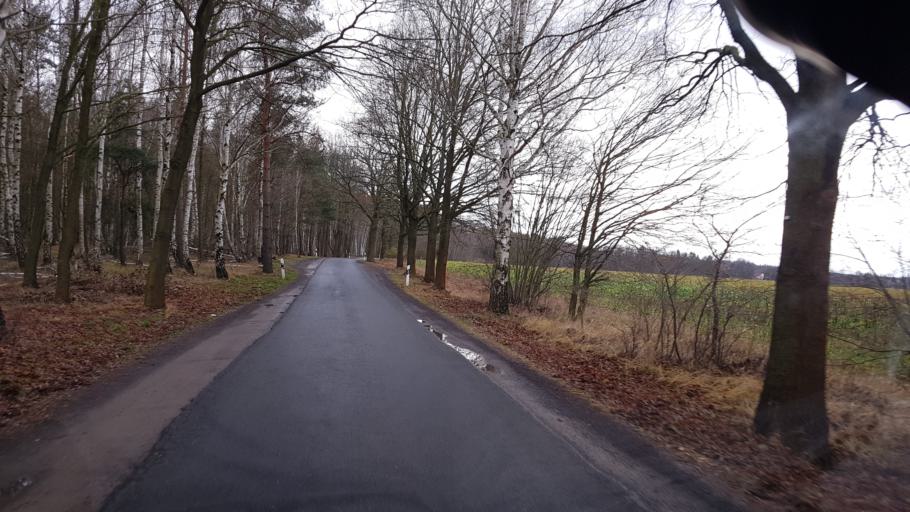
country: DE
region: Brandenburg
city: Altdobern
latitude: 51.6652
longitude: 14.0269
